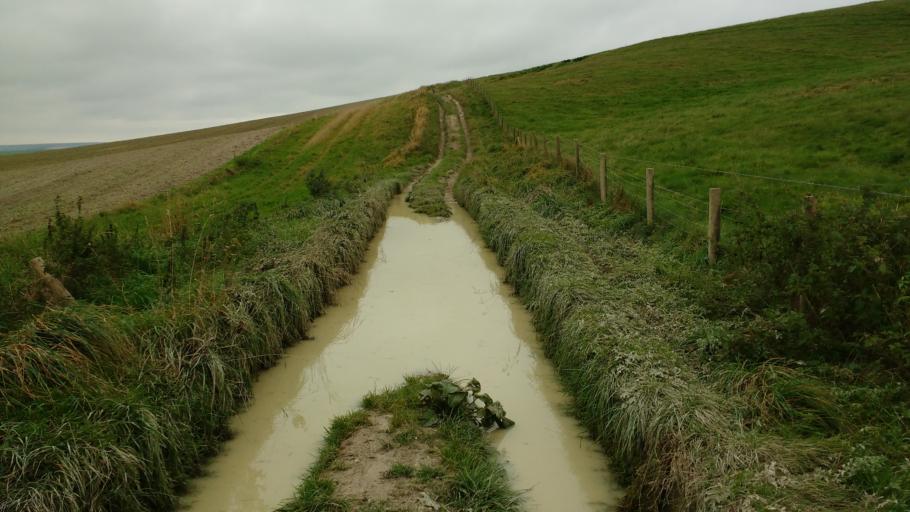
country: GB
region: England
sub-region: Wiltshire
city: Avebury
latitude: 51.4227
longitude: -1.9212
